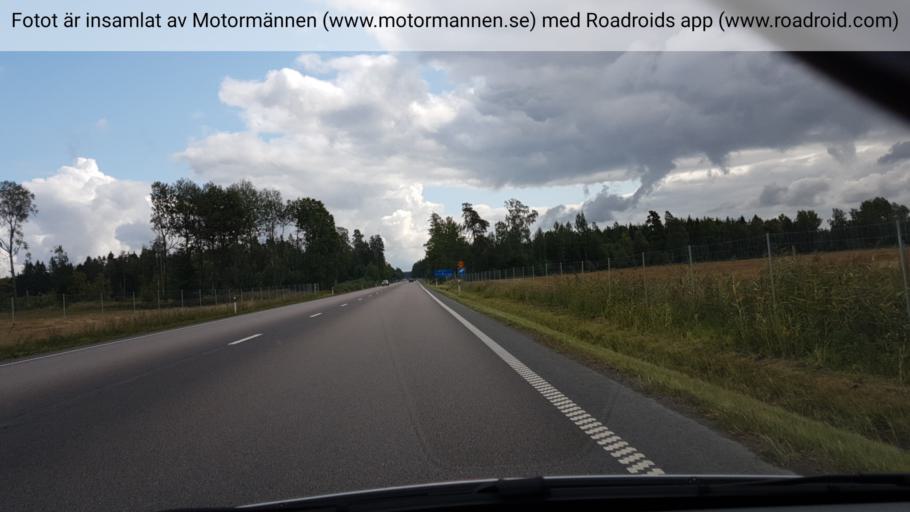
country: SE
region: Vaestra Goetaland
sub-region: Lidkopings Kommun
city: Vinninga
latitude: 58.4669
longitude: 13.2168
